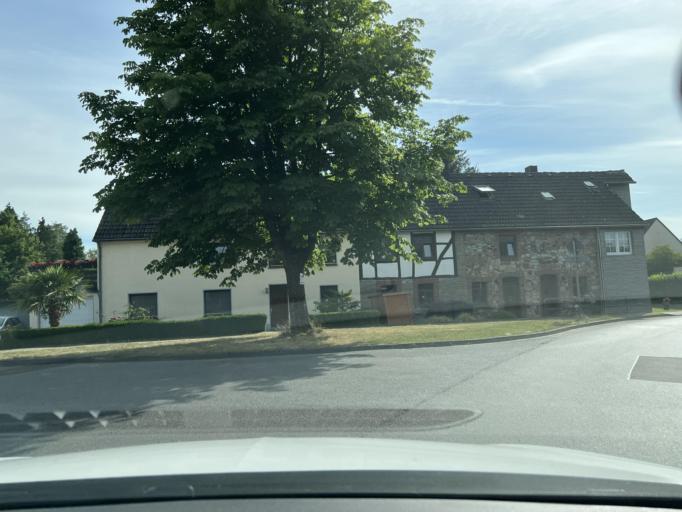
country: DE
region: North Rhine-Westphalia
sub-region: Regierungsbezirk Koln
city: Roetgen
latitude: 50.6886
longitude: 6.1682
